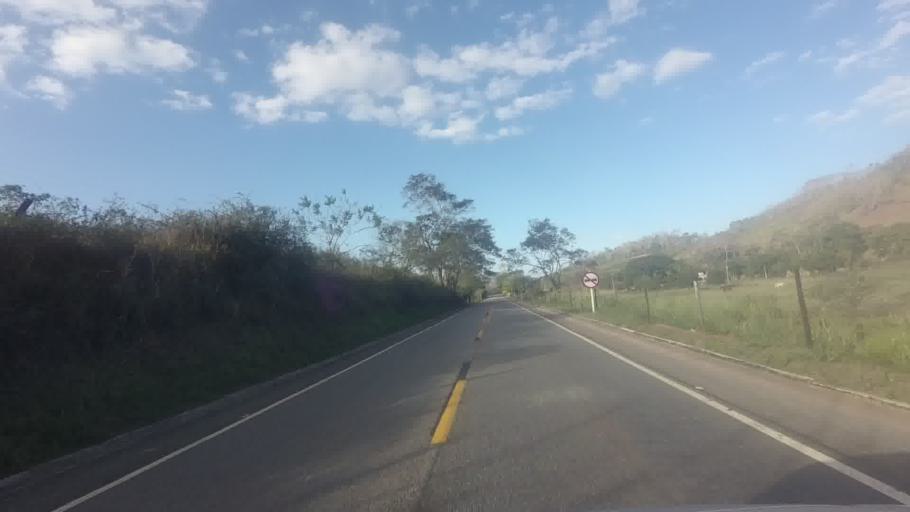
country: BR
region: Espirito Santo
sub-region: Jeronimo Monteiro
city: Jeronimo Monteiro
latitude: -20.9180
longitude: -41.3065
